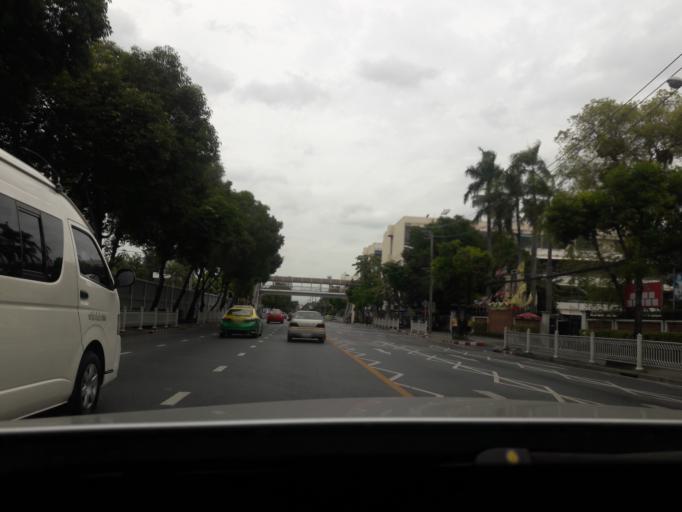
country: TH
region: Bangkok
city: Dusit
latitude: 13.7788
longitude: 100.5154
